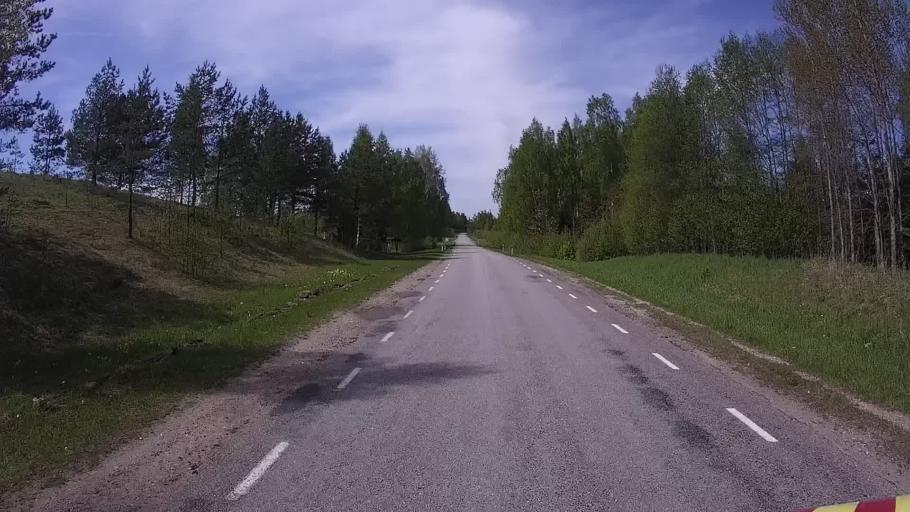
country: EE
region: Vorumaa
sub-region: Antsla vald
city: Vana-Antsla
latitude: 57.6445
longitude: 26.3245
